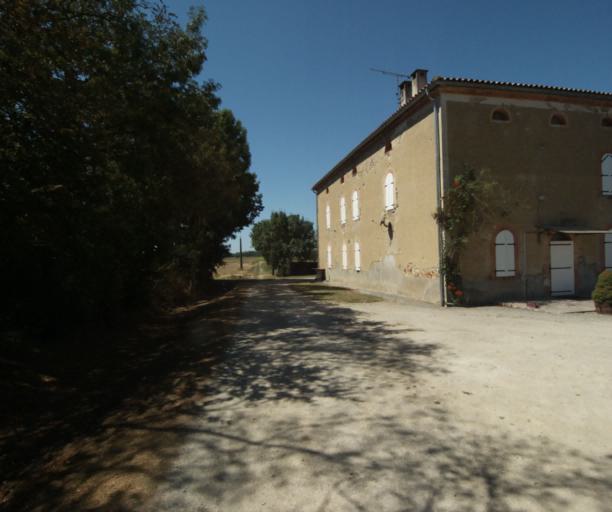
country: FR
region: Midi-Pyrenees
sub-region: Departement de la Haute-Garonne
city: Revel
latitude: 43.4813
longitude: 1.9662
